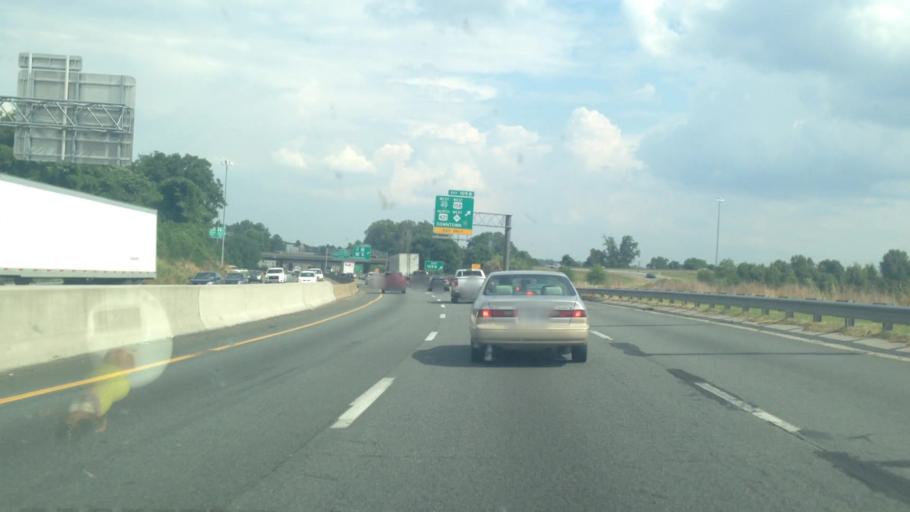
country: US
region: North Carolina
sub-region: Forsyth County
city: Winston-Salem
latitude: 36.0967
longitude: -80.2353
